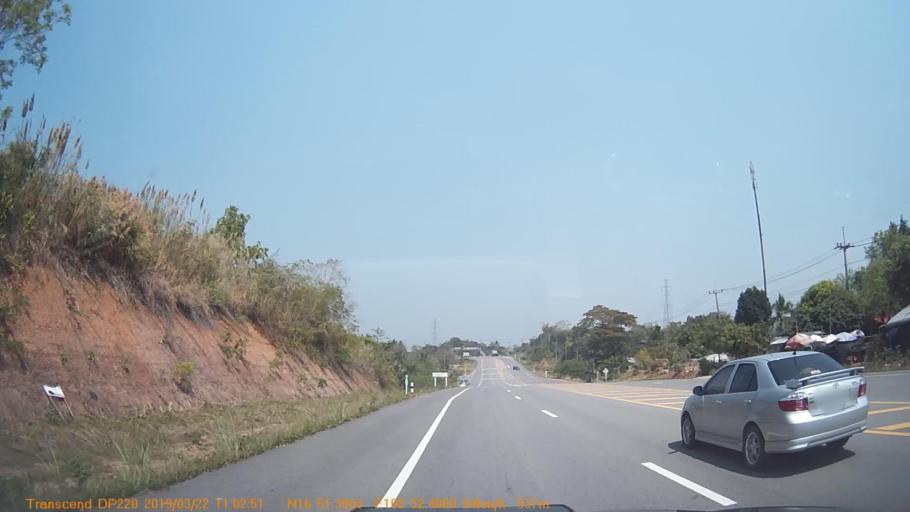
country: TH
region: Phetchabun
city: Khao Kho
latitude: 16.8552
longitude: 100.8734
